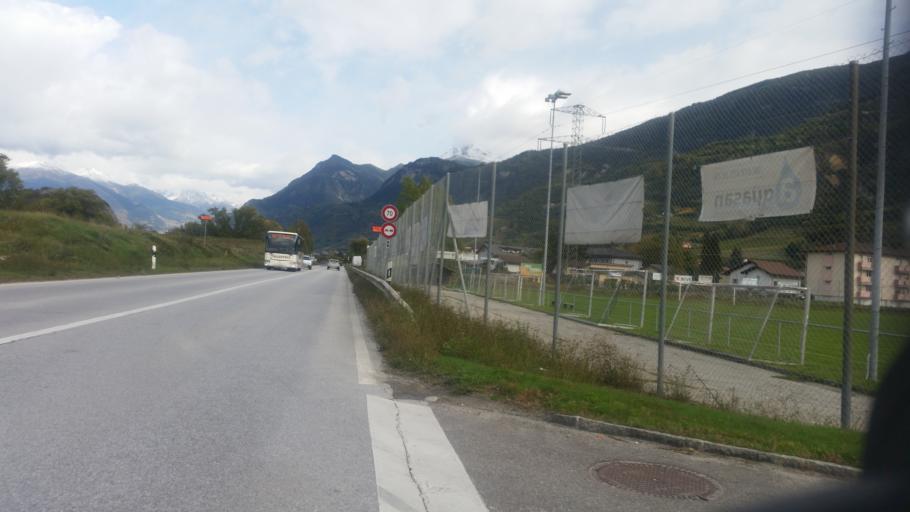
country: CH
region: Valais
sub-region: Sierre District
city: Grone
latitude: 46.2548
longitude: 7.4574
